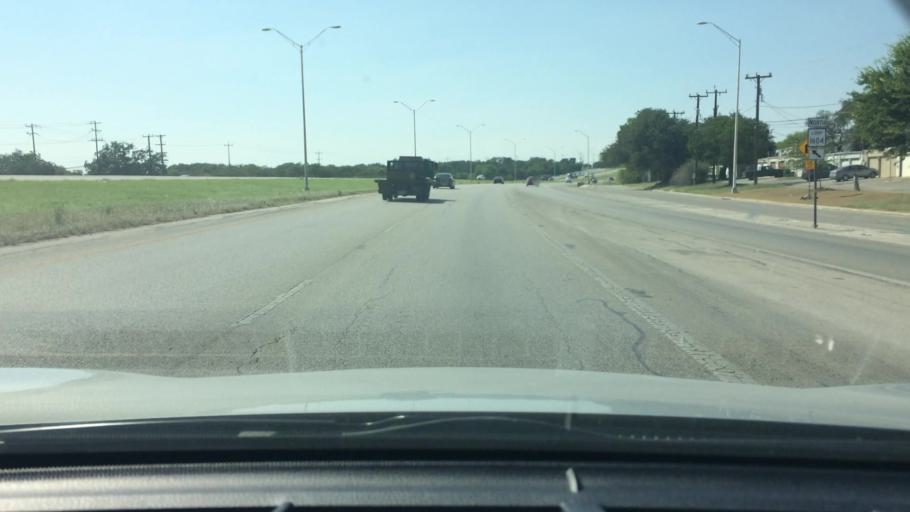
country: US
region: Texas
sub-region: Bexar County
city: Live Oak
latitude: 29.5489
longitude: -98.3182
